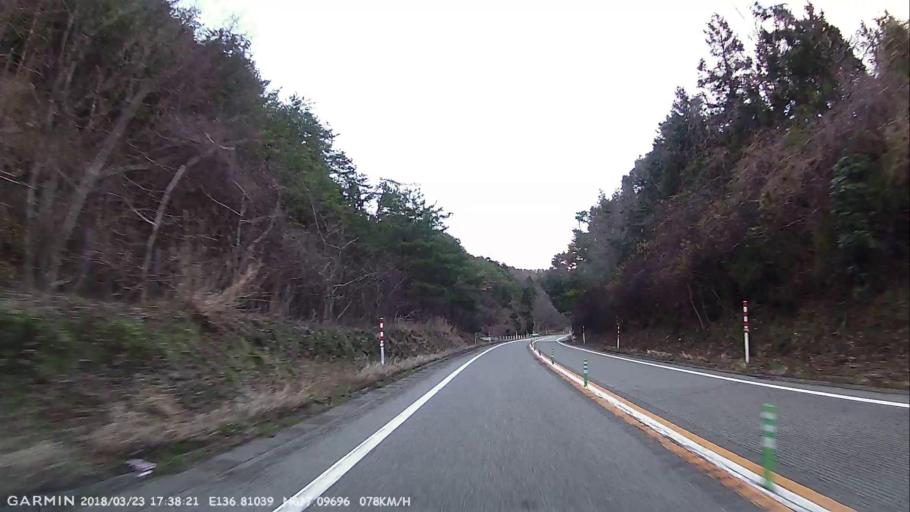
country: JP
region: Ishikawa
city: Nanao
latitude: 37.0971
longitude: 136.8105
